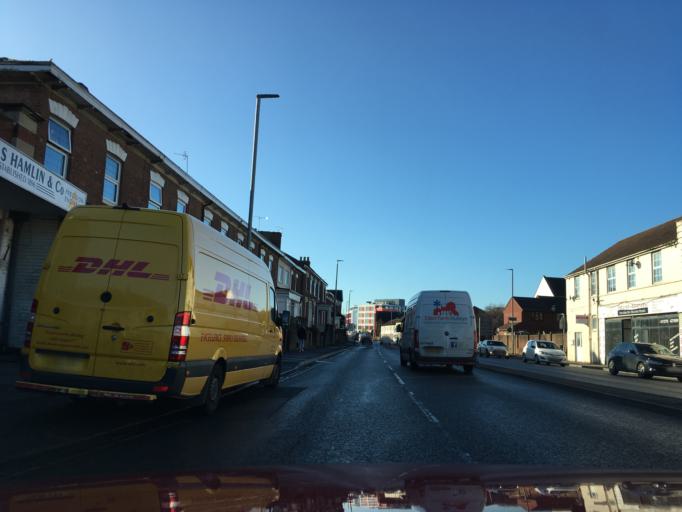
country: GB
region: England
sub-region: Somerset
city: Bridgwater
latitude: 51.1312
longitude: -2.9952
